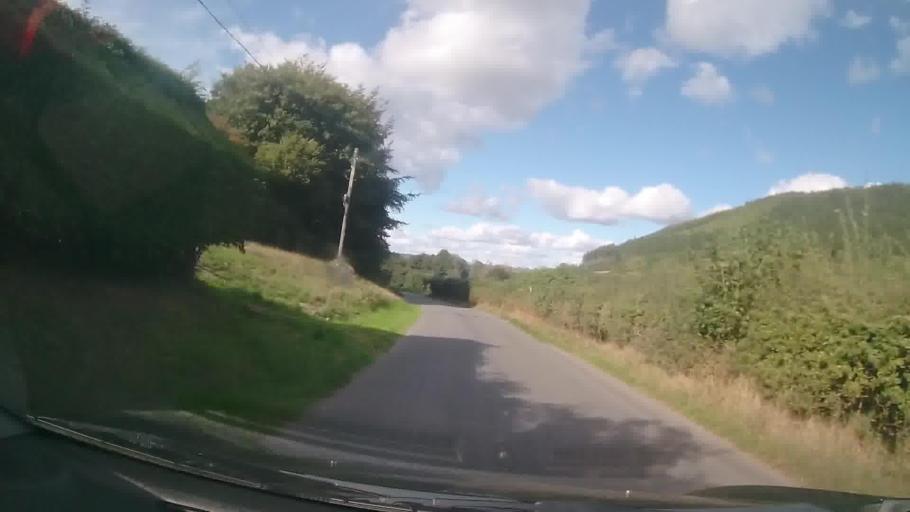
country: GB
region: Wales
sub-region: Sir Powys
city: Brecon
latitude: 51.8783
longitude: -3.3015
